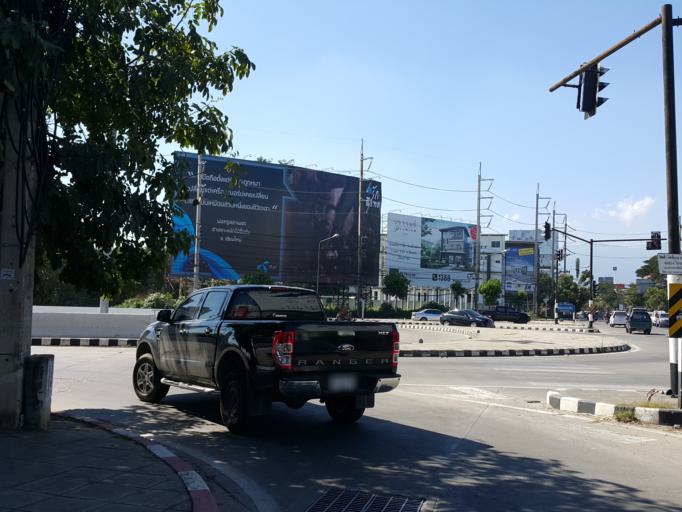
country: TH
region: Chiang Mai
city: Chiang Mai
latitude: 18.7833
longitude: 99.0273
